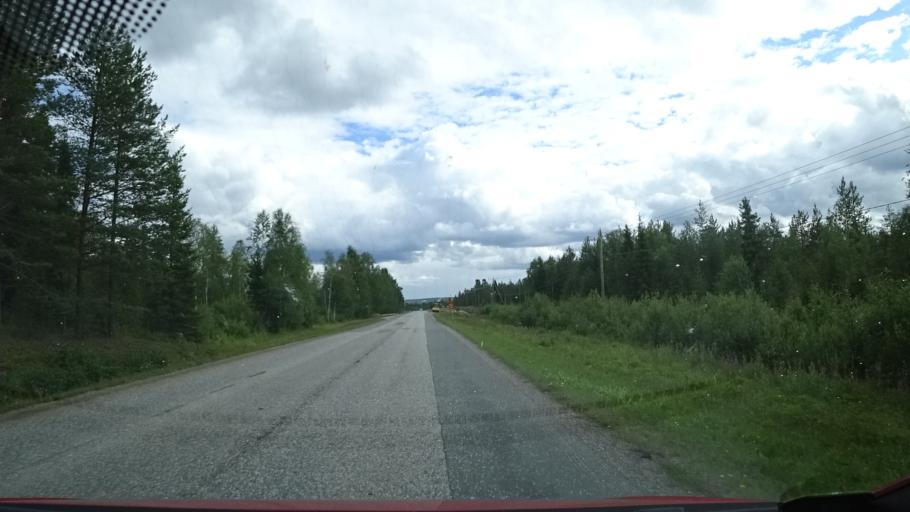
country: FI
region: Lapland
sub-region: Rovaniemi
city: Rovaniemi
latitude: 66.5443
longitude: 25.7100
